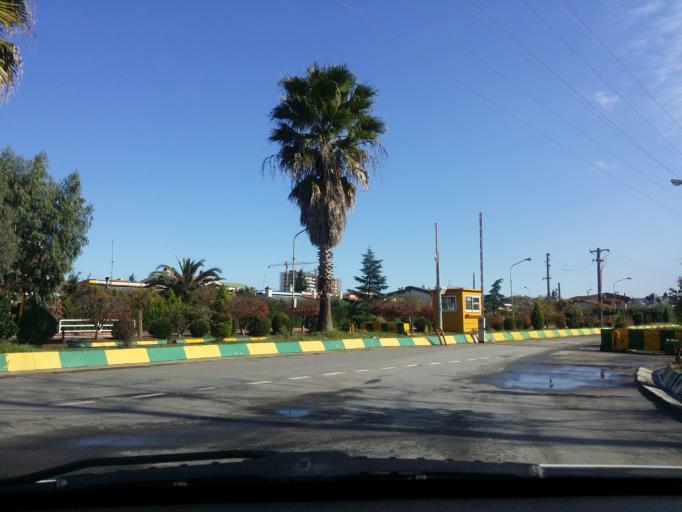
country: IR
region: Mazandaran
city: Chalus
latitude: 36.6754
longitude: 51.3072
